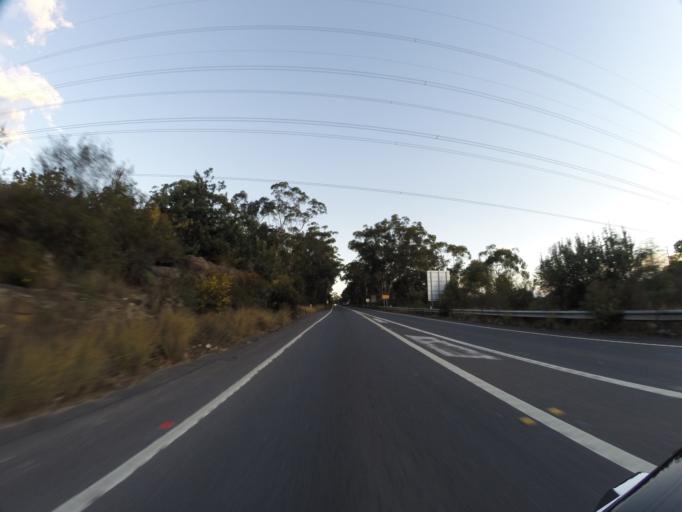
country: AU
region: New South Wales
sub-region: Liverpool
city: East Hills
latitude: -33.9849
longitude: 150.9928
